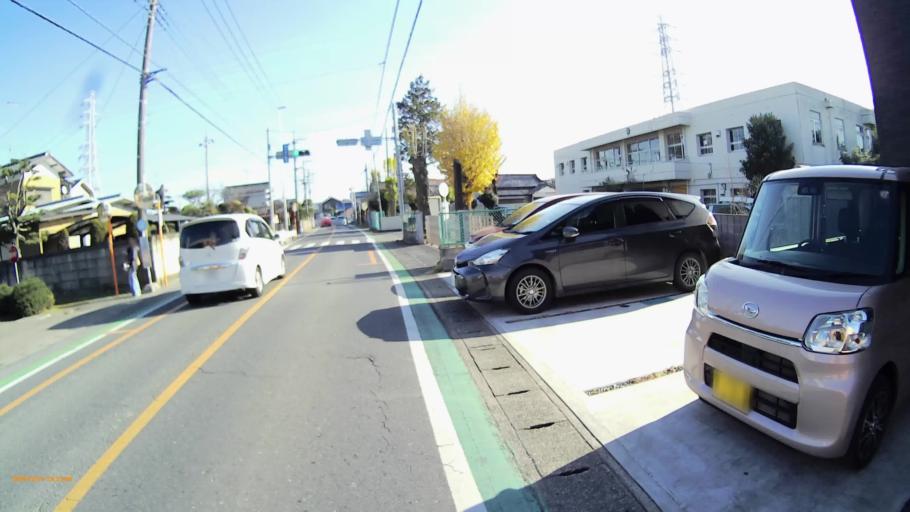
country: JP
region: Saitama
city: Konosu
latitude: 36.0770
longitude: 139.4829
